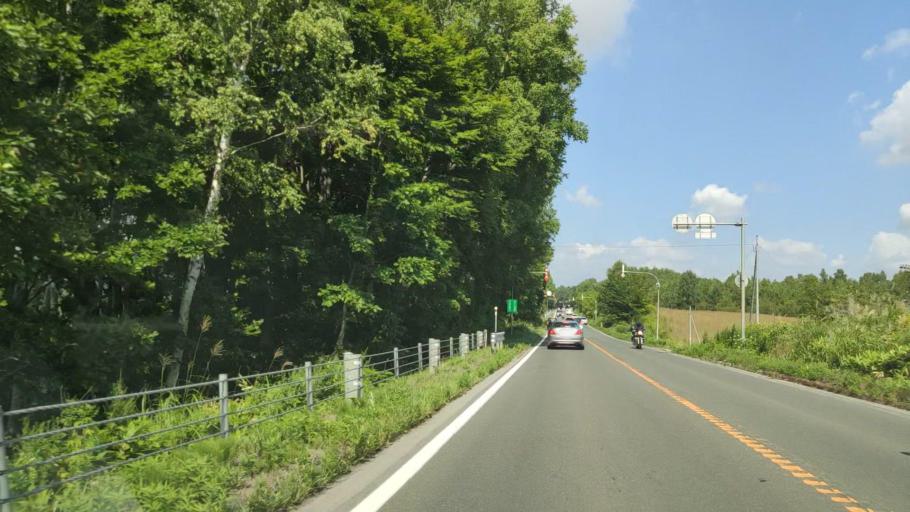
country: JP
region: Hokkaido
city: Shimo-furano
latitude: 43.5068
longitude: 142.4576
